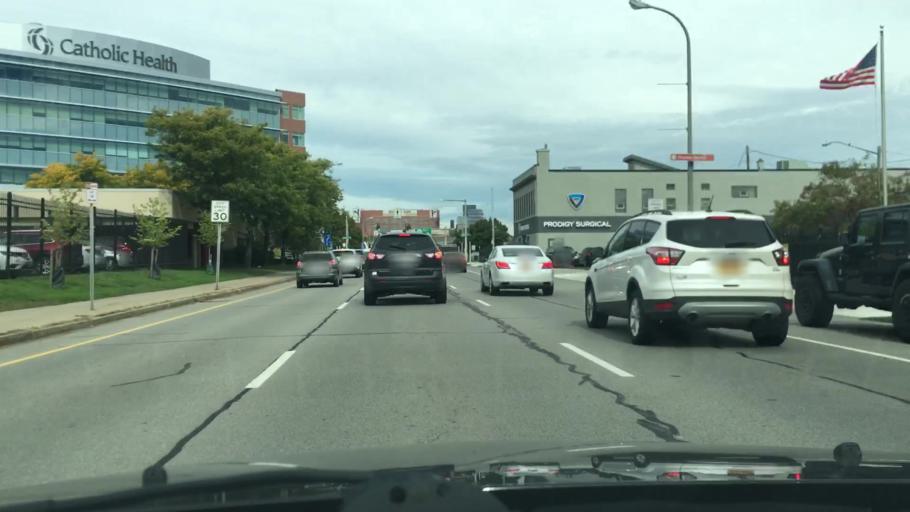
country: US
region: New York
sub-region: Erie County
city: Buffalo
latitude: 42.8894
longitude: -78.8680
